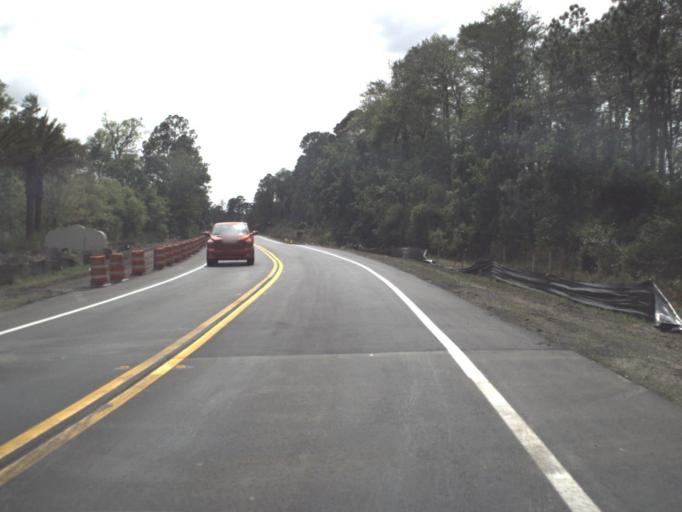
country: US
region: Florida
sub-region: Flagler County
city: Bunnell
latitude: 29.4712
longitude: -81.2707
